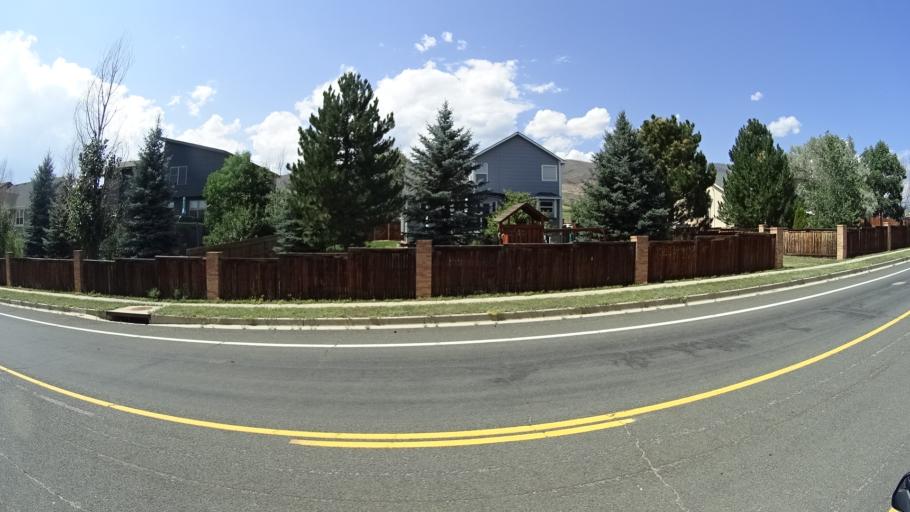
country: US
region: Colorado
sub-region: El Paso County
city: Air Force Academy
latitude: 38.9249
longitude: -104.8669
